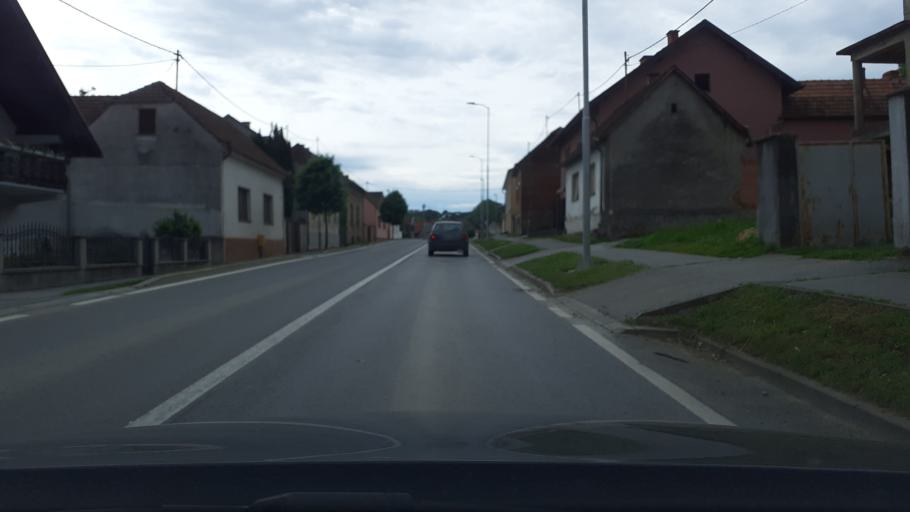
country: HR
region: Pozesko-Slavonska
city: Pleternica
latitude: 45.2909
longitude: 17.8006
